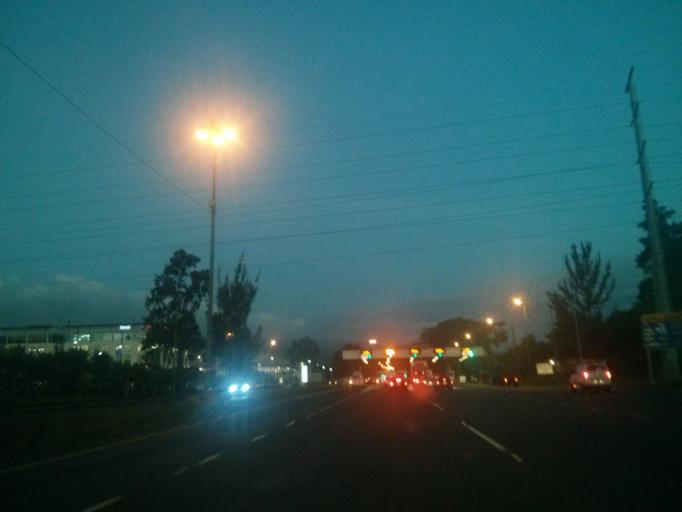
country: CR
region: Cartago
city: San Diego
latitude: 9.9007
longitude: -83.9960
